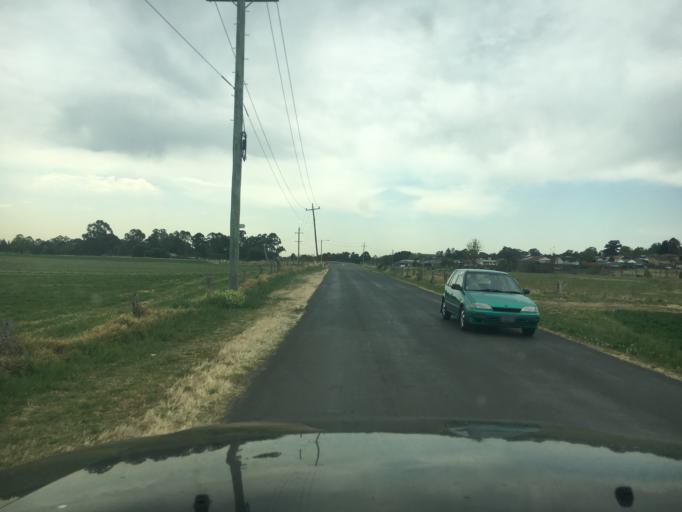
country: AU
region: New South Wales
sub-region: Maitland Municipality
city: East Maitland
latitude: -32.7517
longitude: 151.5705
